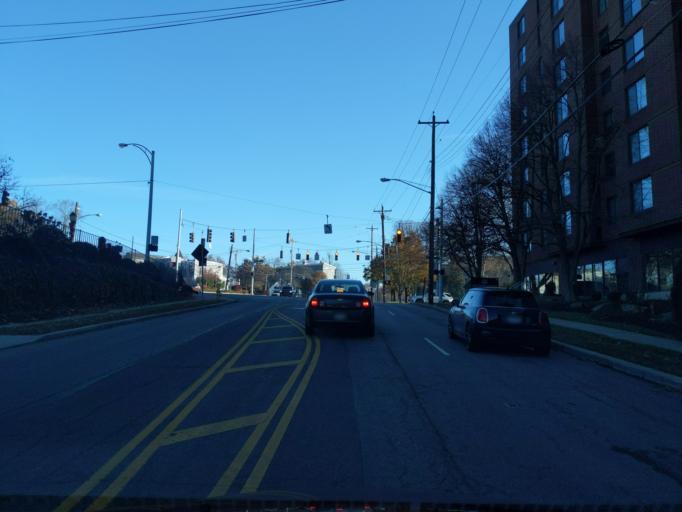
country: US
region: Kentucky
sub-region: Campbell County
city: Dayton
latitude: 39.1319
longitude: -84.4613
